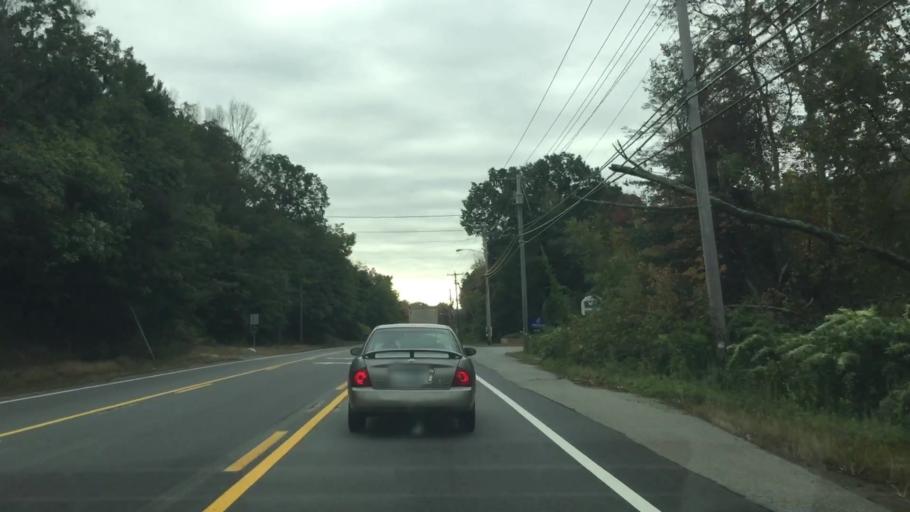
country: US
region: Massachusetts
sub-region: Essex County
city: Andover
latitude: 42.6519
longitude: -71.0964
